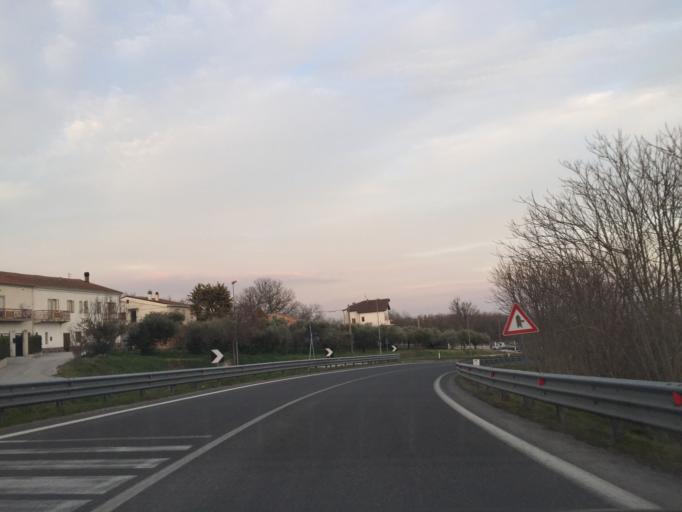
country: IT
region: Molise
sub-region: Provincia di Campobasso
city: Campobasso
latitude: 41.5611
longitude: 14.6980
